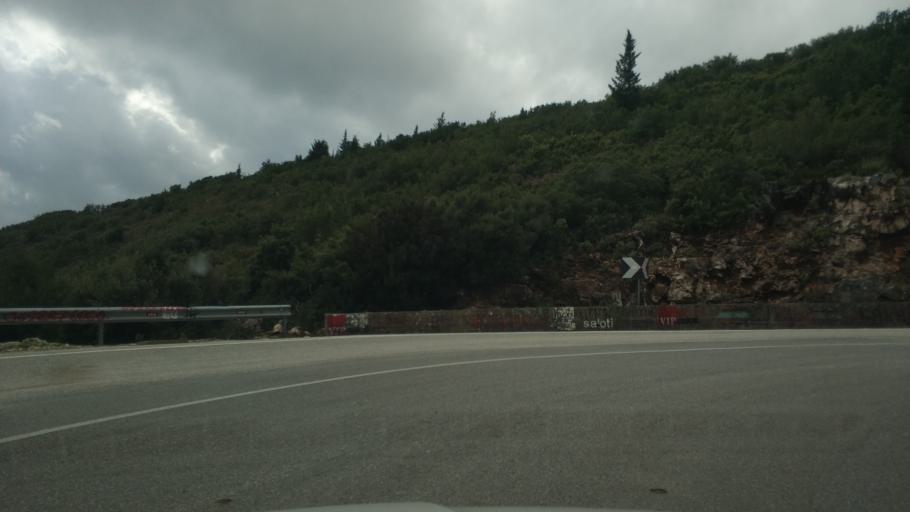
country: AL
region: Vlore
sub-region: Rrethi i Vlores
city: Vranisht
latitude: 40.1398
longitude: 19.6751
